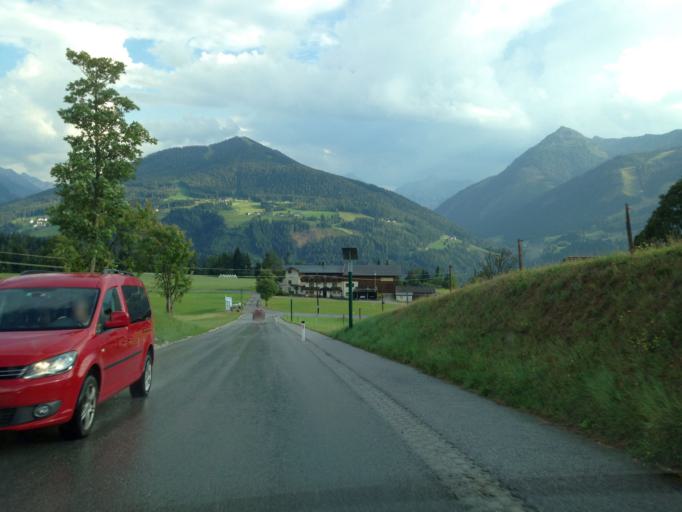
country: AT
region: Styria
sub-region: Politischer Bezirk Liezen
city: Schladming
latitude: 47.4010
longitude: 13.6196
